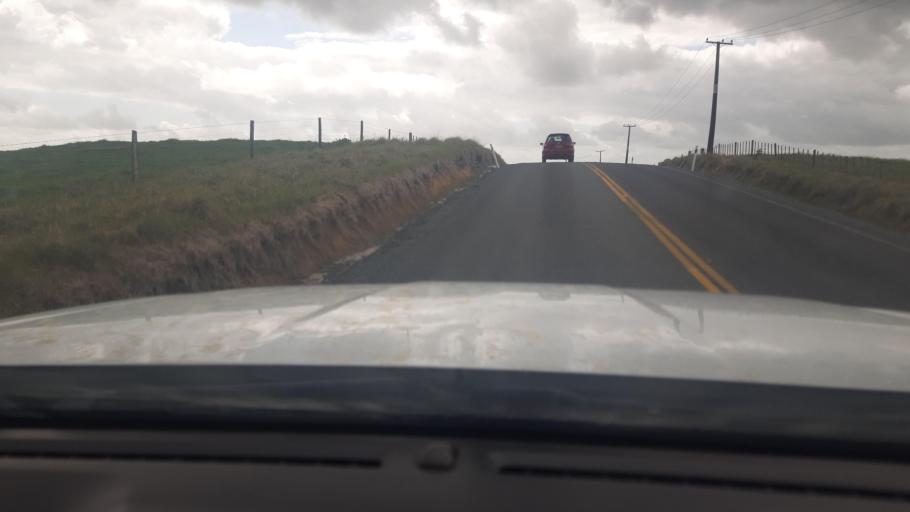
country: NZ
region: Northland
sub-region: Far North District
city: Kaitaia
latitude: -35.0510
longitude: 173.3231
